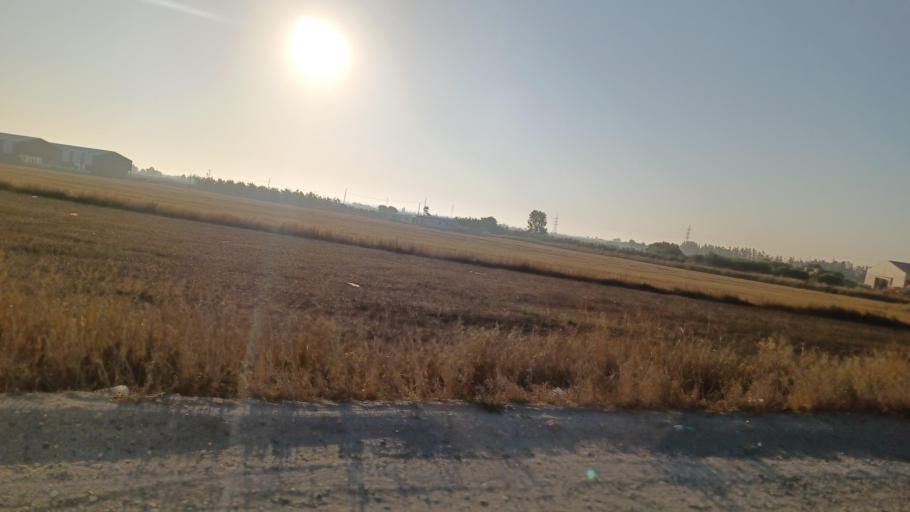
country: CY
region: Ammochostos
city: Avgorou
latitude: 35.0112
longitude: 33.8036
